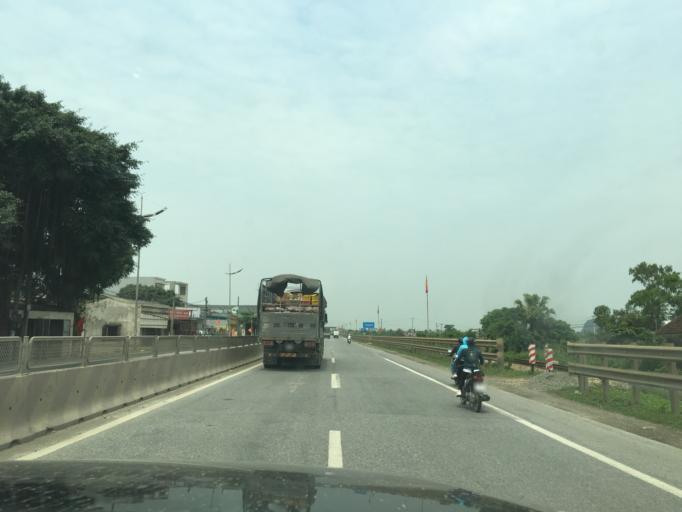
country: VN
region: Ninh Binh
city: Thi Tran Tam Diep
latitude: 20.1726
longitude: 105.9445
